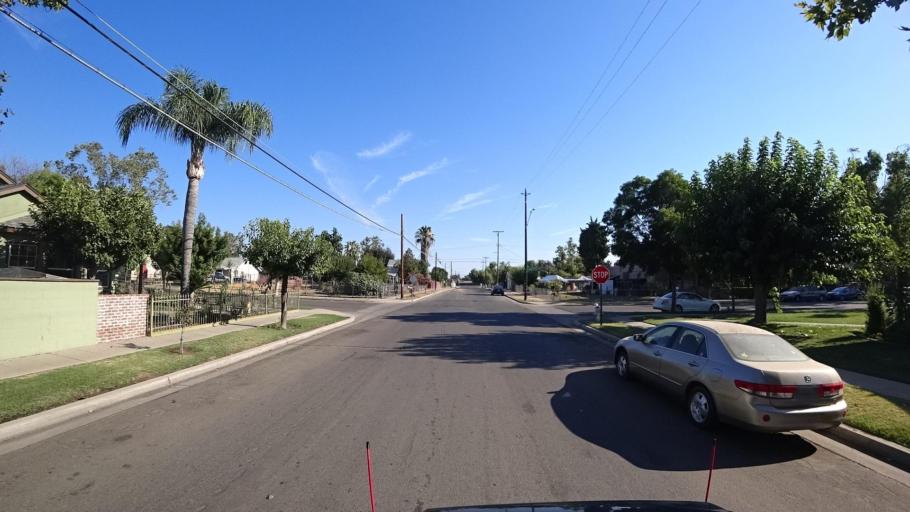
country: US
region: California
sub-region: Fresno County
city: Fresno
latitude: 36.7484
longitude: -119.7676
